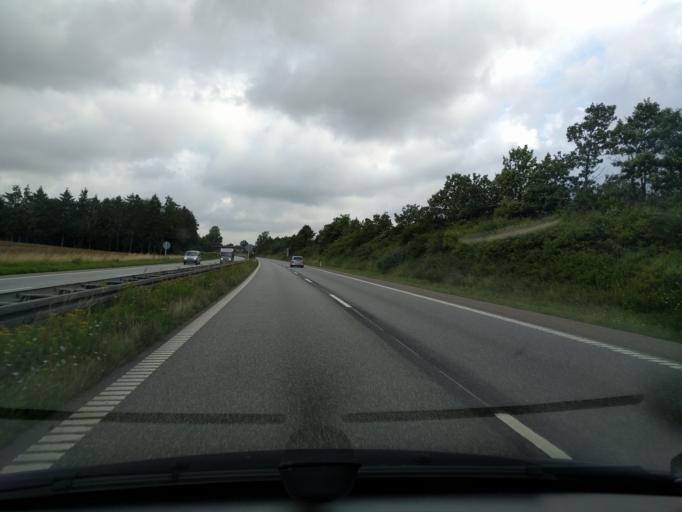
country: DK
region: Zealand
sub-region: Vordingborg Kommune
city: Nyrad
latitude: 54.9764
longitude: 12.0047
